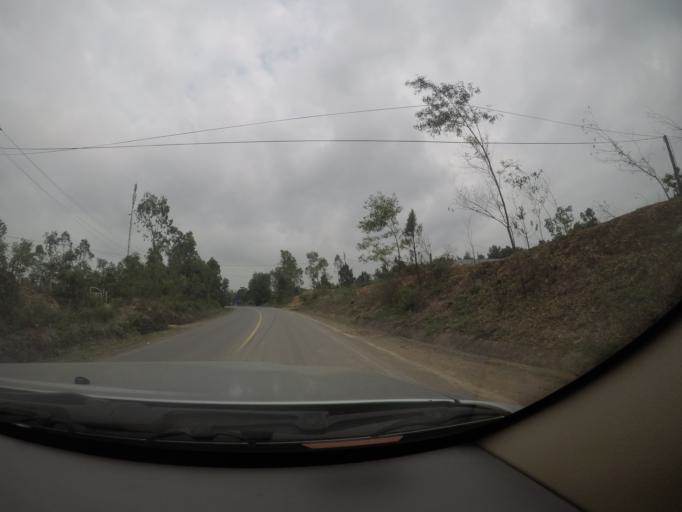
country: VN
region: Quang Binh
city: Quan Hau
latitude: 17.3849
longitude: 106.6119
